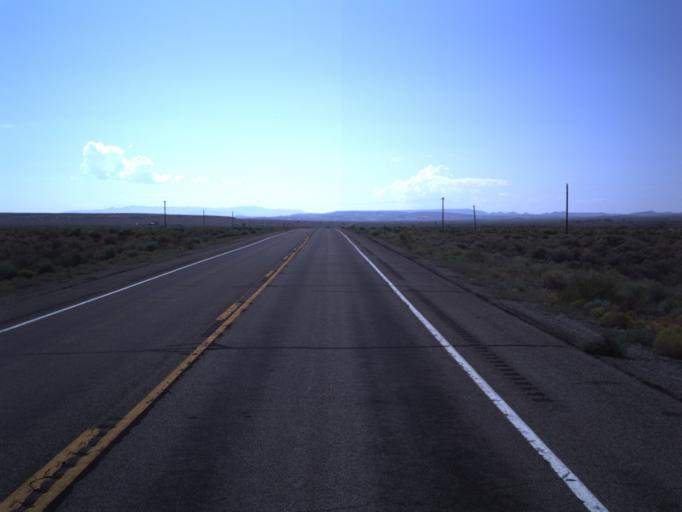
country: US
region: Utah
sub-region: San Juan County
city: Blanding
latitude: 37.1852
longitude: -109.5916
